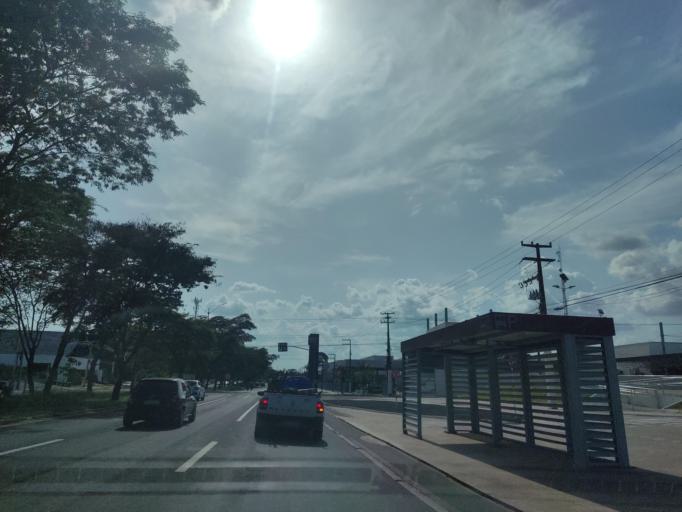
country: BR
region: Piaui
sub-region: Teresina
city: Teresina
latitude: -5.0812
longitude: -42.7653
